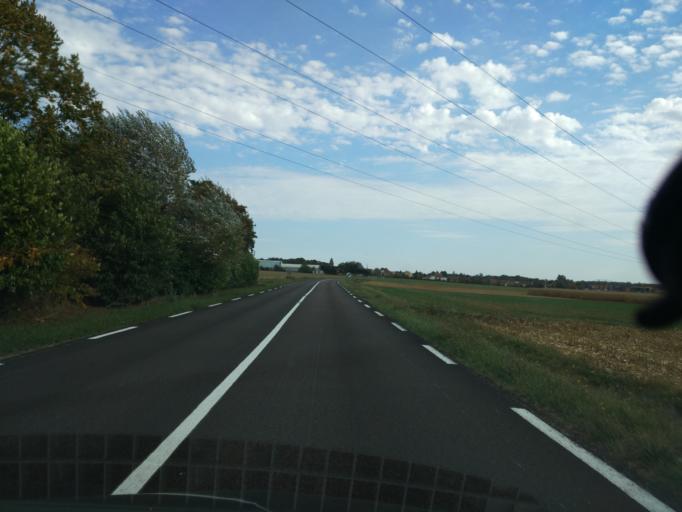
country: FR
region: Ile-de-France
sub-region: Departement de l'Essonne
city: Gometz-la-Ville
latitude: 48.6741
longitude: 2.1111
